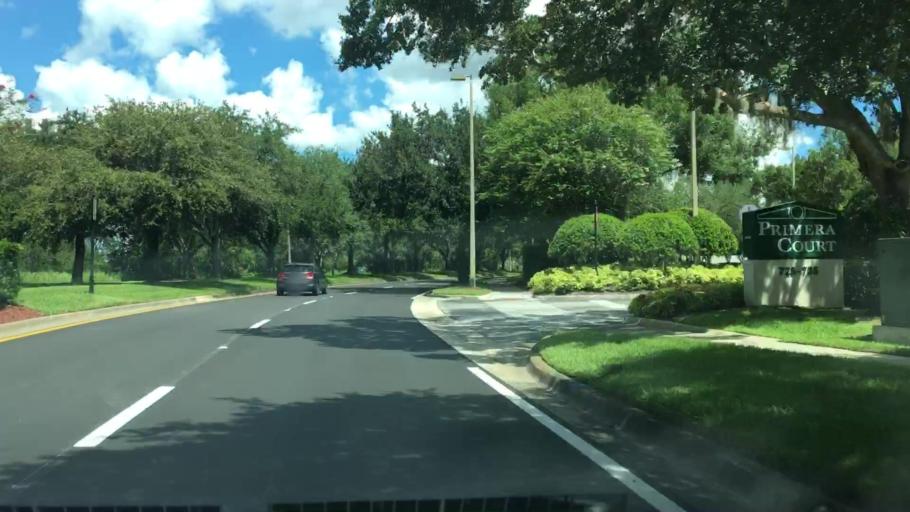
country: US
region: Florida
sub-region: Seminole County
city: Heathrow
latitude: 28.7641
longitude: -81.3539
